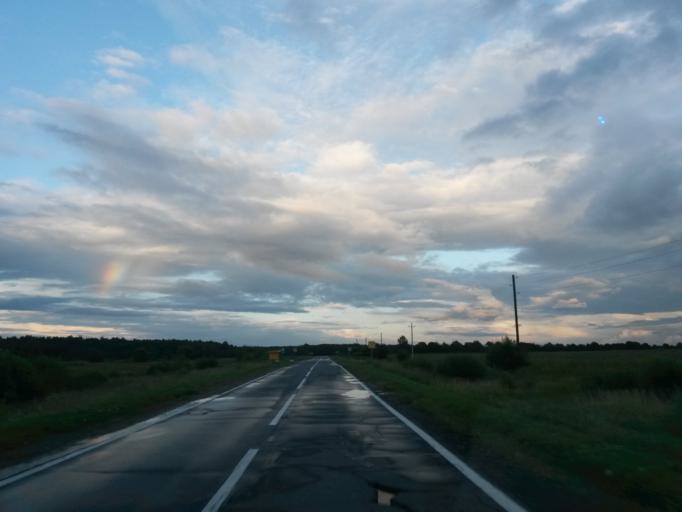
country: RU
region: Jaroslavl
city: Tutayev
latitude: 57.9480
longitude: 39.4762
